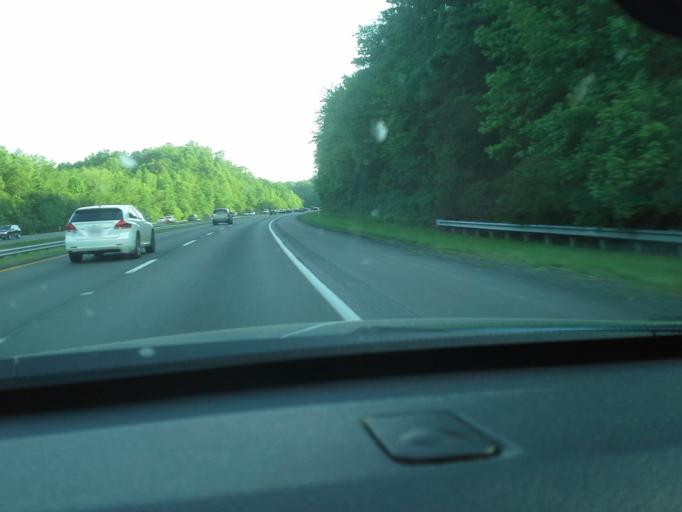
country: US
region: Maryland
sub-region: Anne Arundel County
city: Crownsville
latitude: 39.0328
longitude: -76.6129
